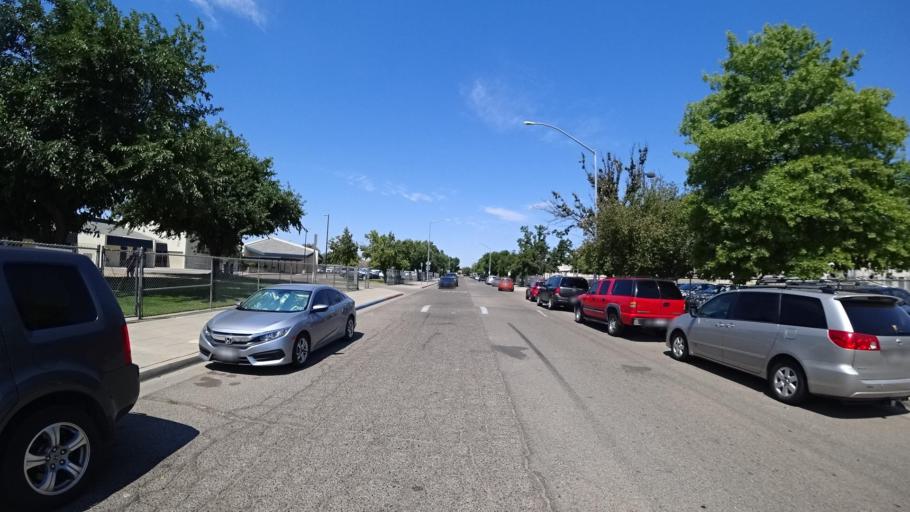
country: US
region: California
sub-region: Fresno County
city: Sunnyside
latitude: 36.7314
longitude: -119.7147
